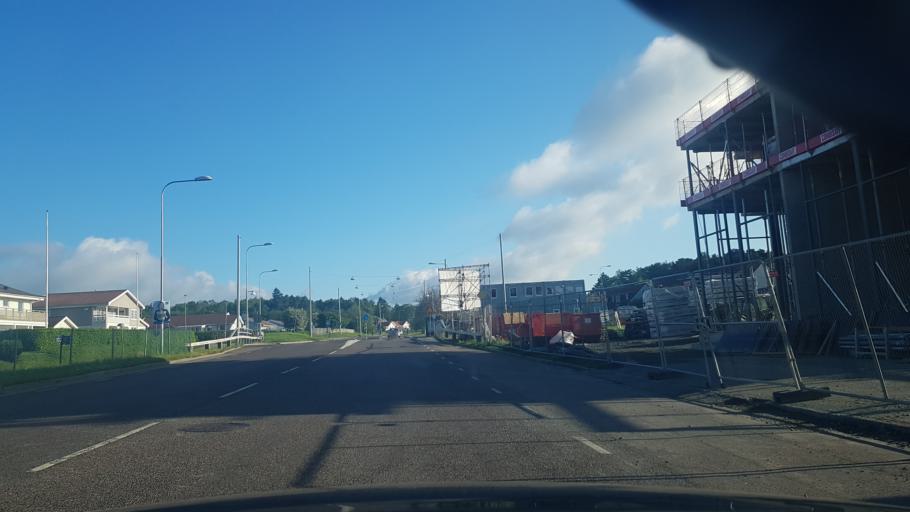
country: SE
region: Vaestra Goetaland
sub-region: Goteborg
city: Majorna
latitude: 57.6415
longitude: 11.8810
